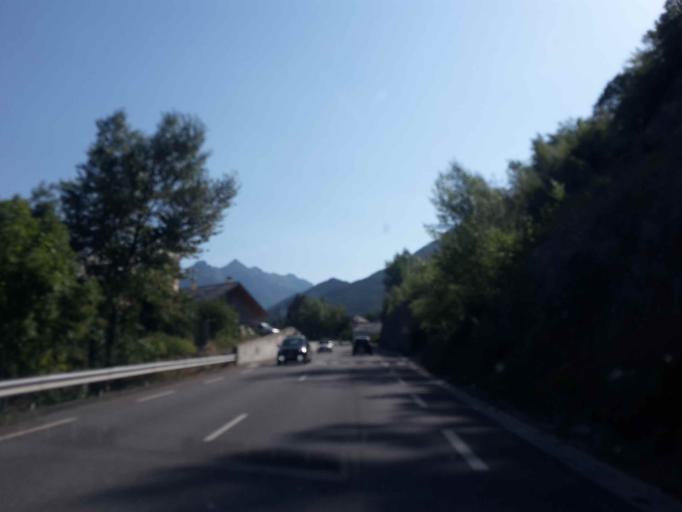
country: FR
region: Provence-Alpes-Cote d'Azur
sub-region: Departement des Hautes-Alpes
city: Guillestre
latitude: 44.6580
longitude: 6.6474
